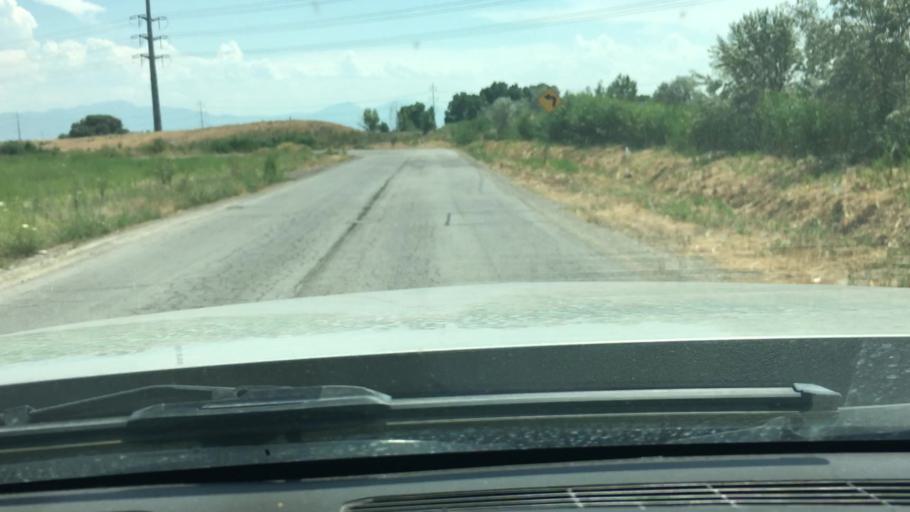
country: US
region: Utah
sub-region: Utah County
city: American Fork
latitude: 40.3450
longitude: -111.7744
